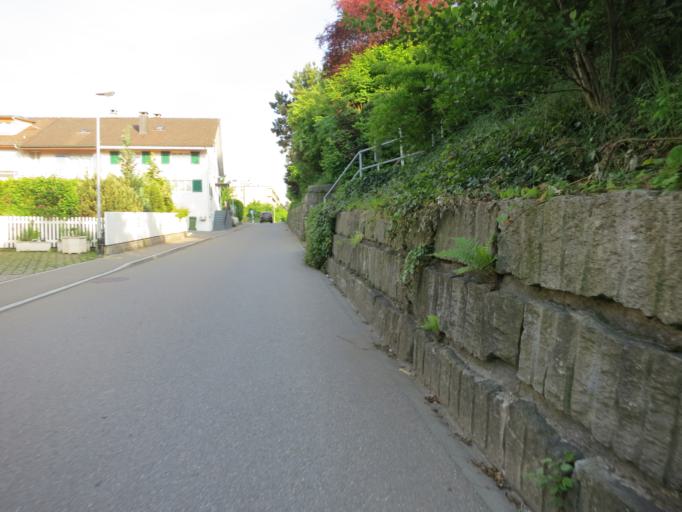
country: CH
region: Zurich
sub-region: Bezirk Hinwil
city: Gossau
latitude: 47.3061
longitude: 8.7560
